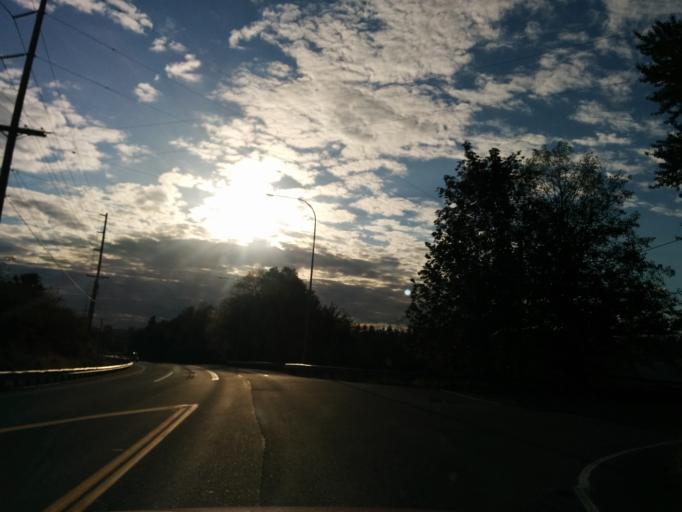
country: US
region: Washington
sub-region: Snohomish County
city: Woods Creek
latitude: 47.8556
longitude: -121.8989
